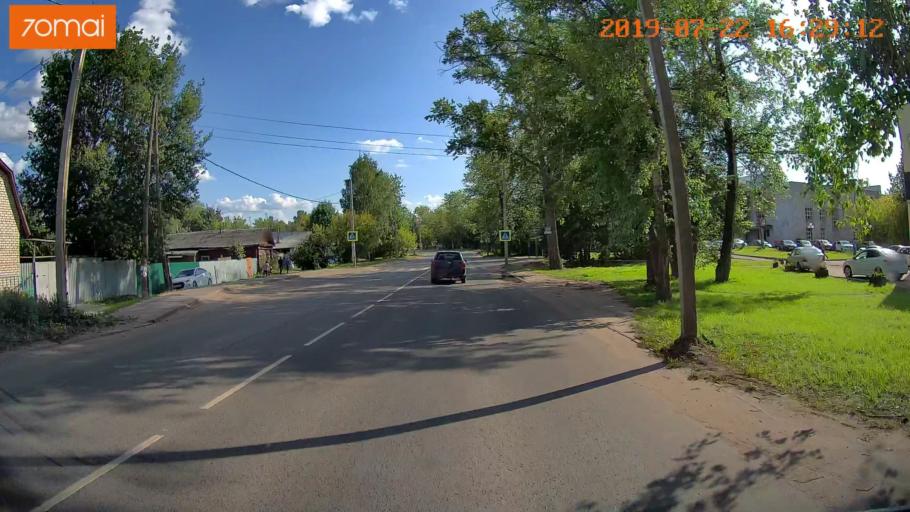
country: RU
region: Ivanovo
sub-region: Gorod Ivanovo
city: Ivanovo
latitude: 57.0329
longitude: 40.9486
